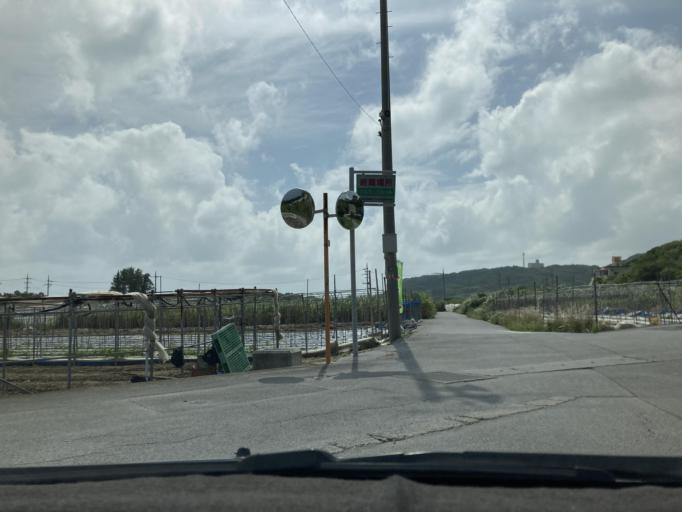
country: JP
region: Okinawa
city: Ginowan
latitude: 26.1500
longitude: 127.8045
